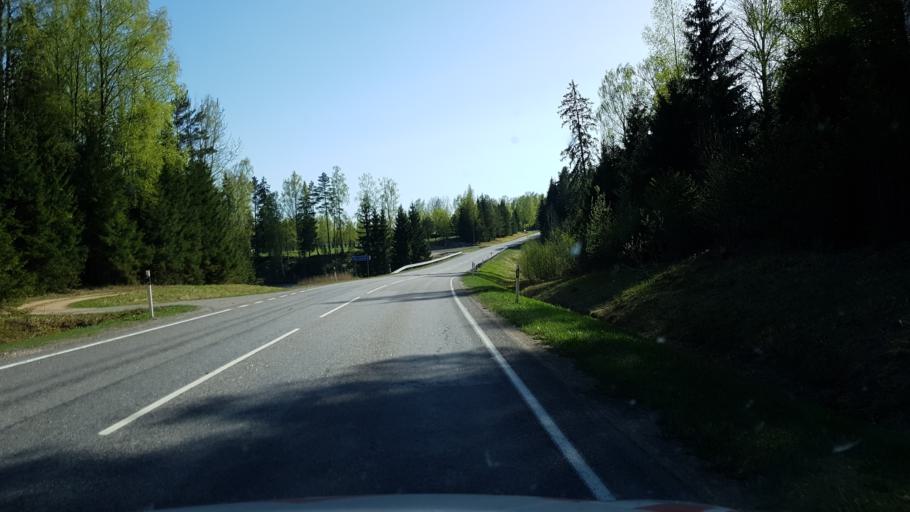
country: EE
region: Paernumaa
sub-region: Saarde vald
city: Kilingi-Nomme
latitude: 58.1841
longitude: 25.0533
